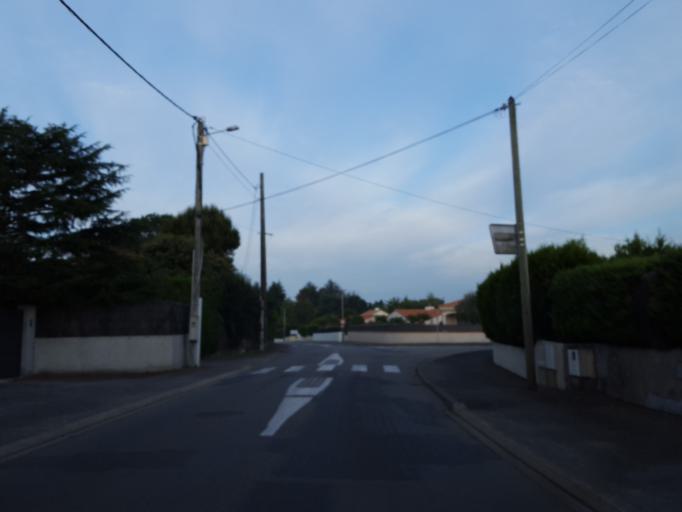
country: FR
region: Pays de la Loire
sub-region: Departement de la Loire-Atlantique
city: Basse-Goulaine
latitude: 47.2010
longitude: -1.4708
